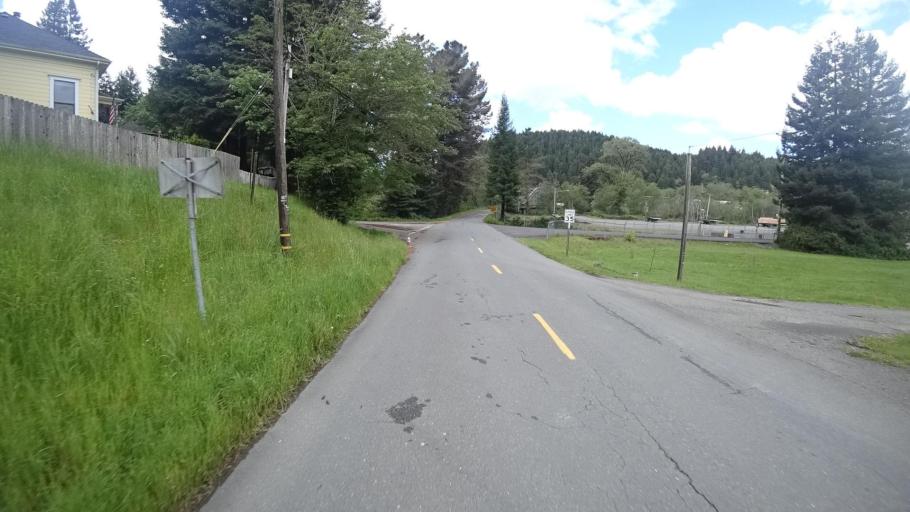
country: US
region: California
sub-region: Humboldt County
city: Blue Lake
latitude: 40.8700
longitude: -123.9593
